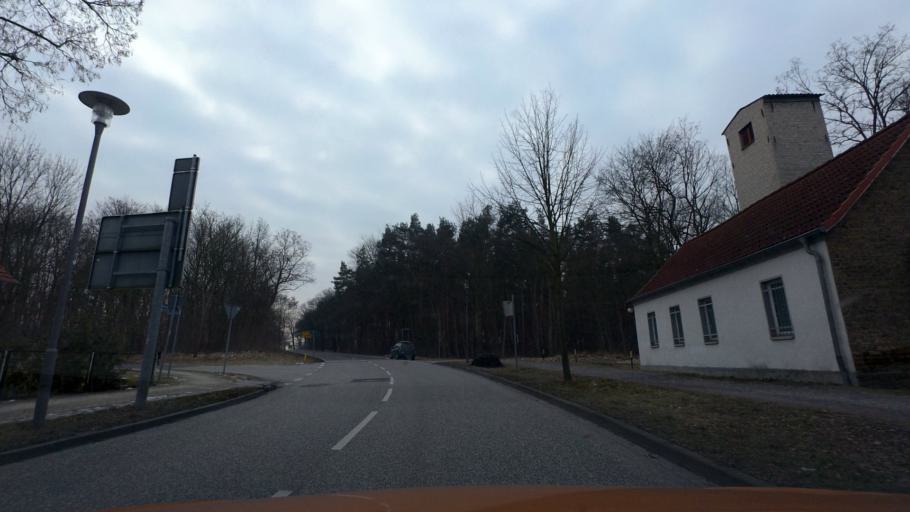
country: DE
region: Brandenburg
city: Ludwigsfelde
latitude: 52.2823
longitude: 13.2111
